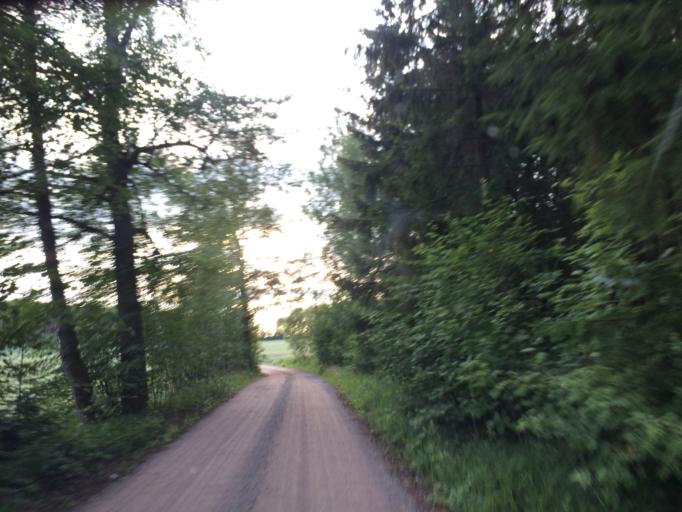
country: FI
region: Haeme
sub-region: Haemeenlinna
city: Janakkala
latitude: 60.8933
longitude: 24.6136
